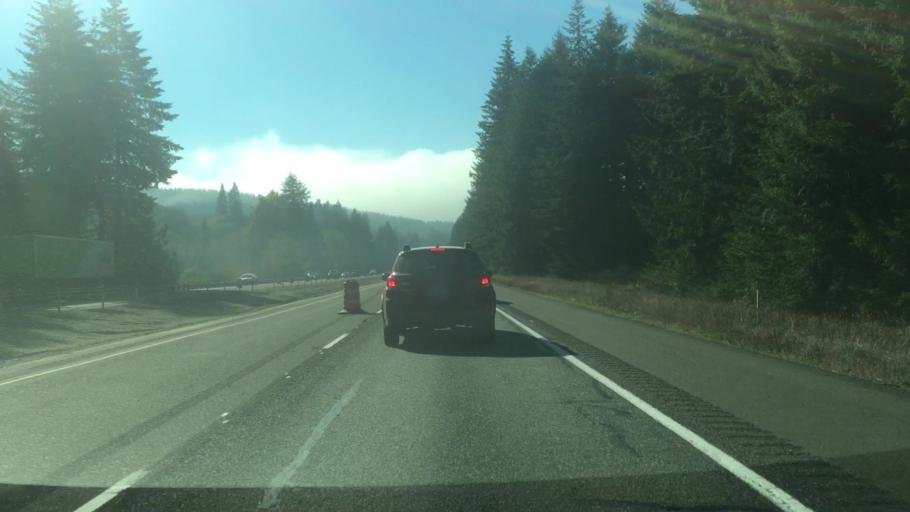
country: US
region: Washington
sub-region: Grays Harbor County
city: McCleary
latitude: 47.0467
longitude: -123.3117
